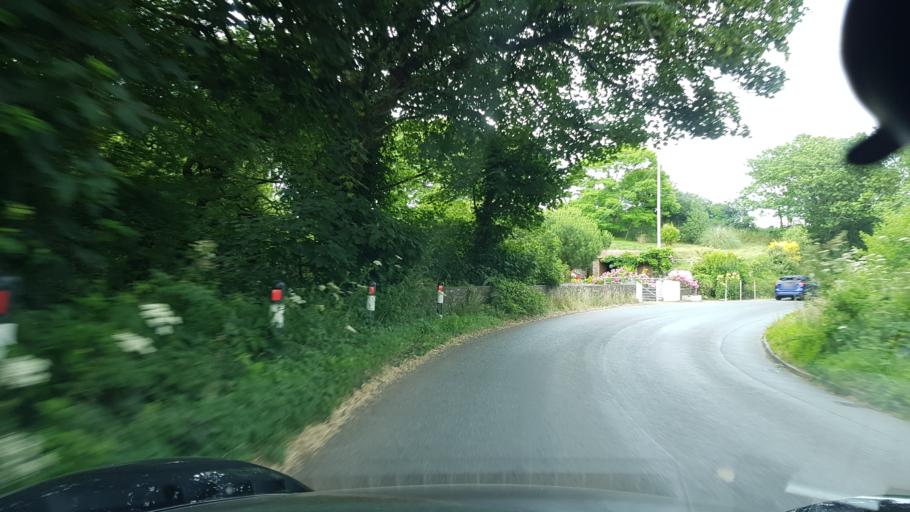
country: GB
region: Wales
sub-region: Pembrokeshire
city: Herbrandston
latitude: 51.7653
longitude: -5.0770
